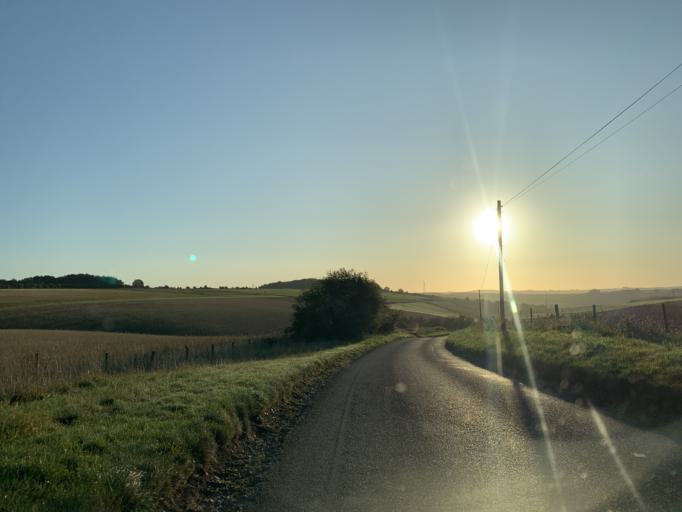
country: GB
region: England
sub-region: Wiltshire
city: Woodford
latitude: 51.1283
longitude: -1.8535
